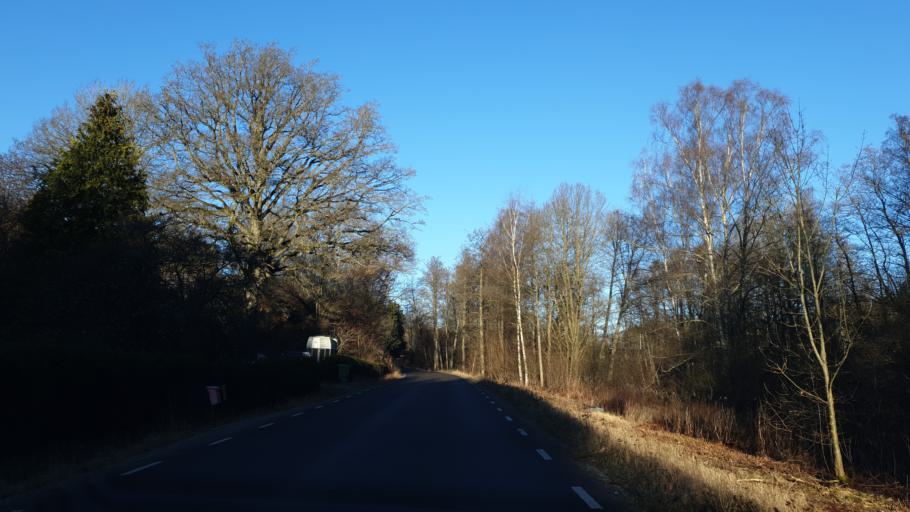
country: SE
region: Blekinge
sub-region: Karlskrona Kommun
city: Nattraby
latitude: 56.2544
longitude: 15.5132
